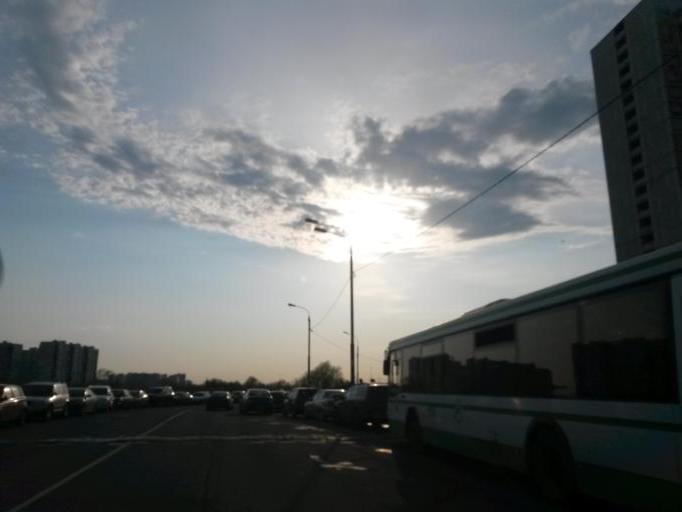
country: RU
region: Moscow
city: Brateyevo
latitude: 55.6321
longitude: 37.7436
